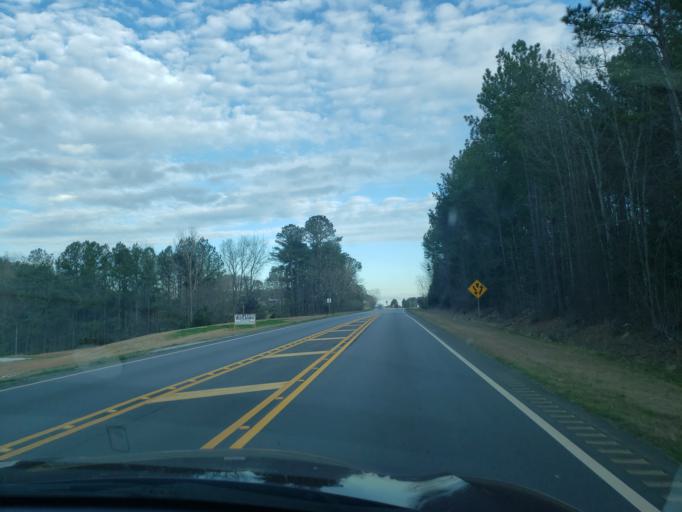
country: US
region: Alabama
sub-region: Randolph County
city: Wedowee
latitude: 33.2868
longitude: -85.4725
